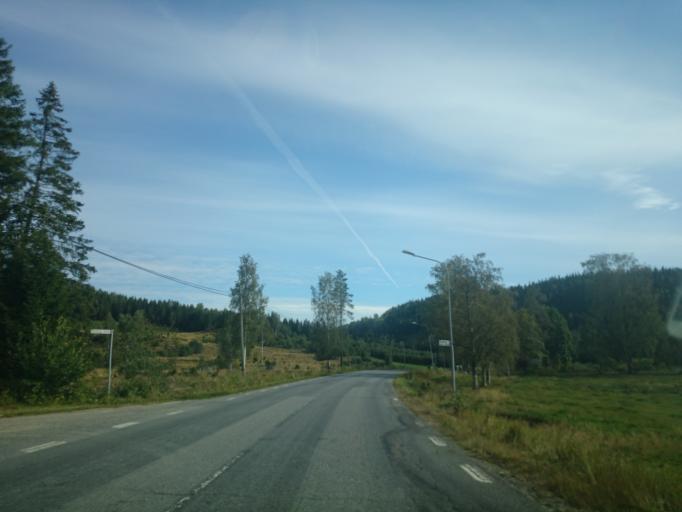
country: SE
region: Vaesternorrland
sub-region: Kramfors Kommun
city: Nordingra
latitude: 62.9235
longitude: 18.2045
